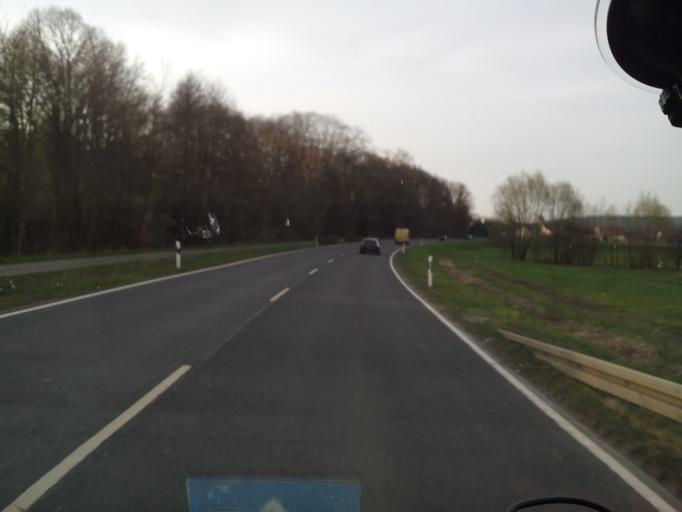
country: DE
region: Bavaria
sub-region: Upper Franconia
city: Reckendorf
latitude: 50.0115
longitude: 10.8273
